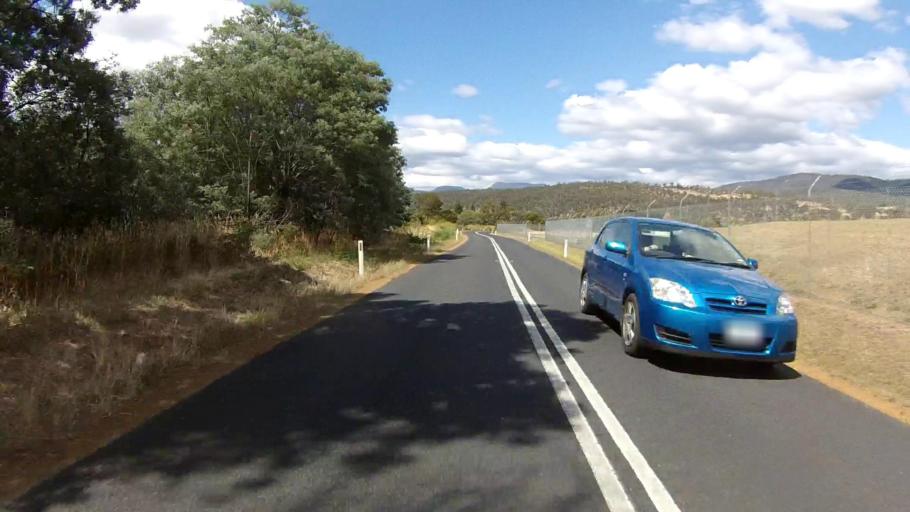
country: AU
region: Tasmania
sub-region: Derwent Valley
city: New Norfolk
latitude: -42.7689
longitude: 147.0249
